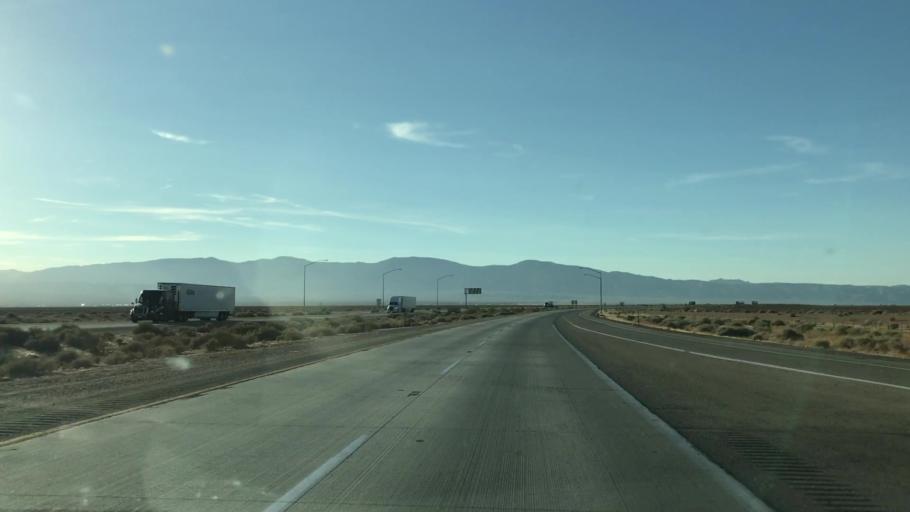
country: US
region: California
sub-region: Kern County
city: Mojave
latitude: 35.0408
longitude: -118.1091
